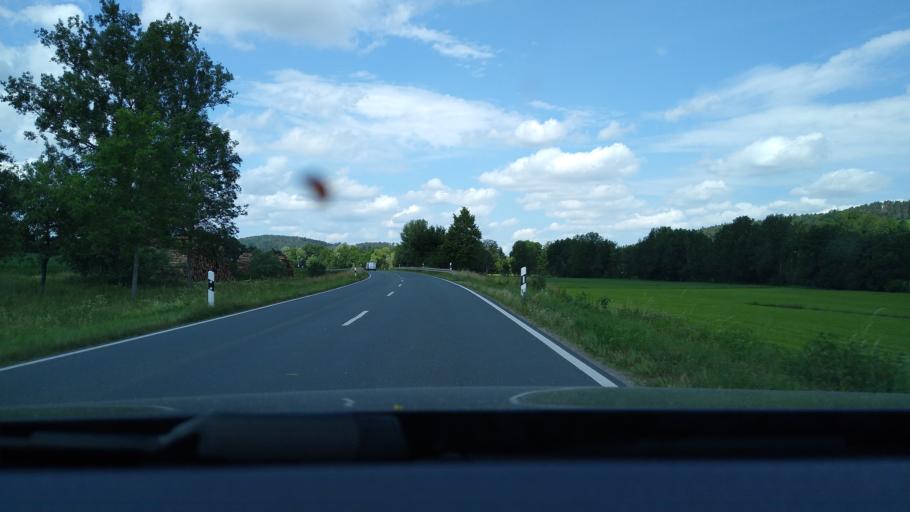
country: DE
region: Bavaria
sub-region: Regierungsbezirk Mittelfranken
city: Trautskirchen
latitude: 49.4605
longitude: 10.5726
